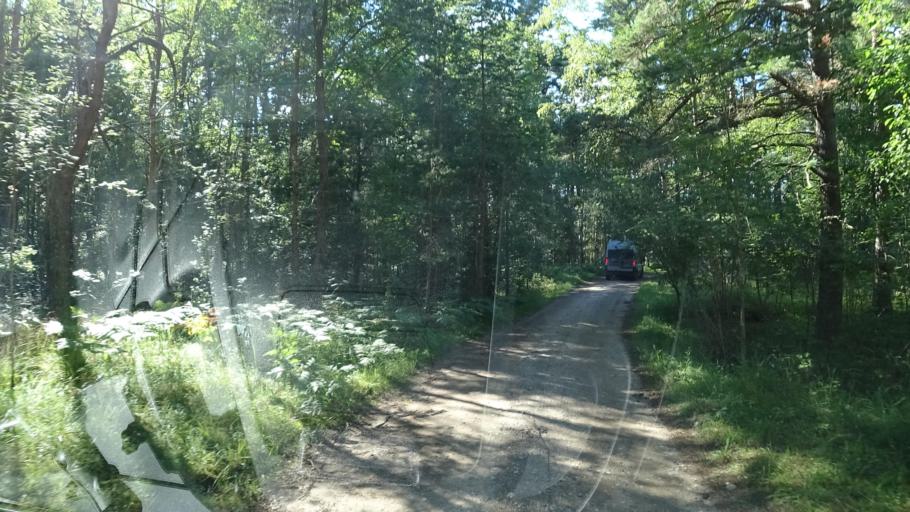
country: LV
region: Ventspils
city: Ventspils
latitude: 57.4871
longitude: 21.6486
